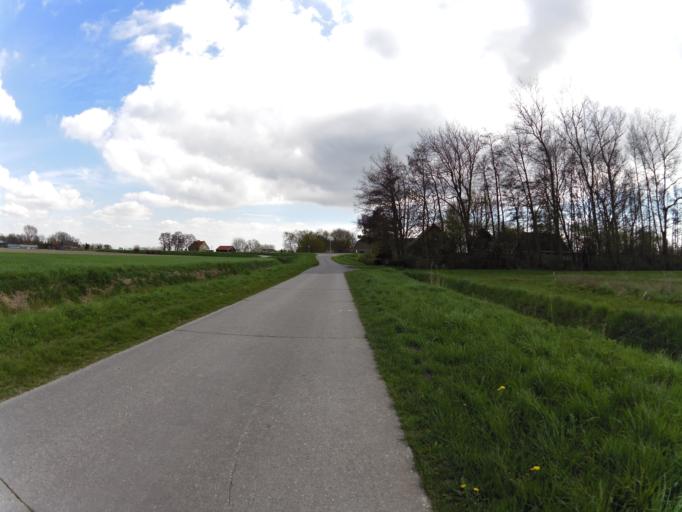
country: NL
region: South Holland
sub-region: Gemeente Hellevoetsluis
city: Nieuwenhoorn
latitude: 51.8815
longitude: 4.1239
